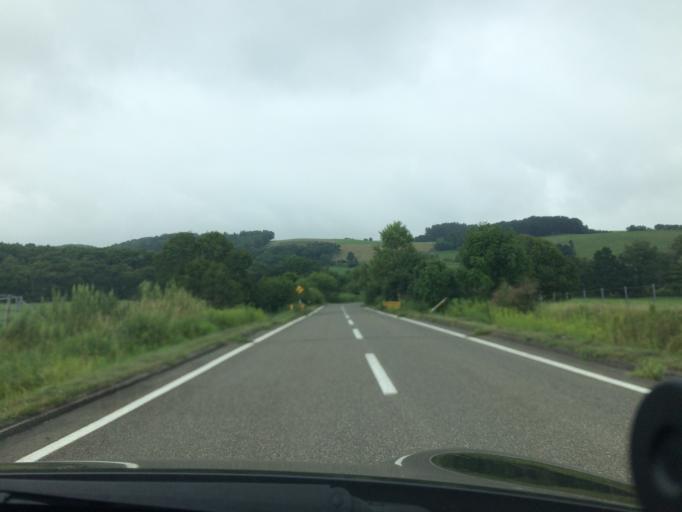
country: JP
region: Hokkaido
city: Otofuke
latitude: 43.0026
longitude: 143.0815
